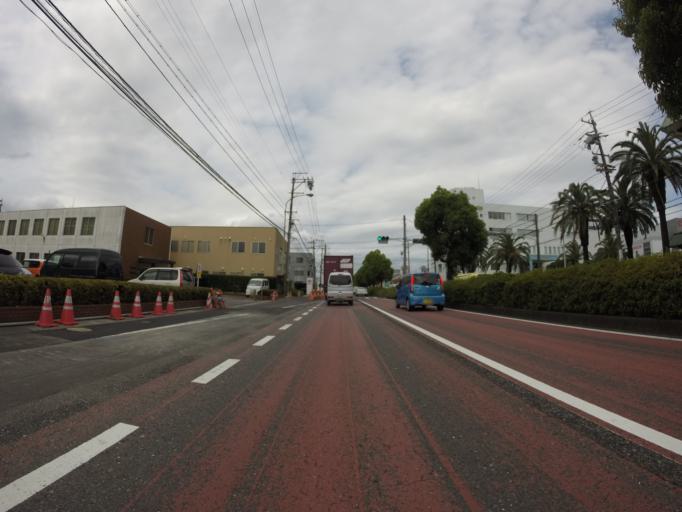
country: JP
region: Shizuoka
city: Shizuoka-shi
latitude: 34.9983
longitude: 138.4299
